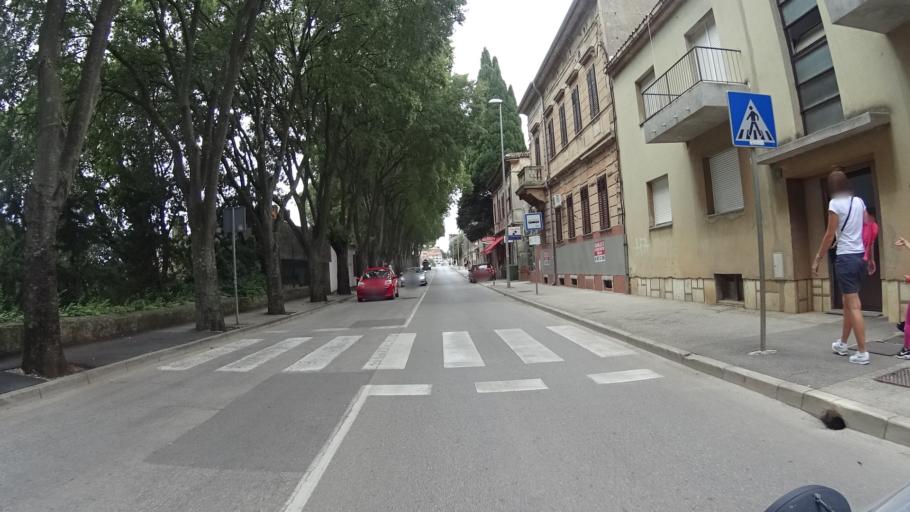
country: HR
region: Istarska
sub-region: Grad Pula
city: Pula
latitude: 44.8640
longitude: 13.8550
